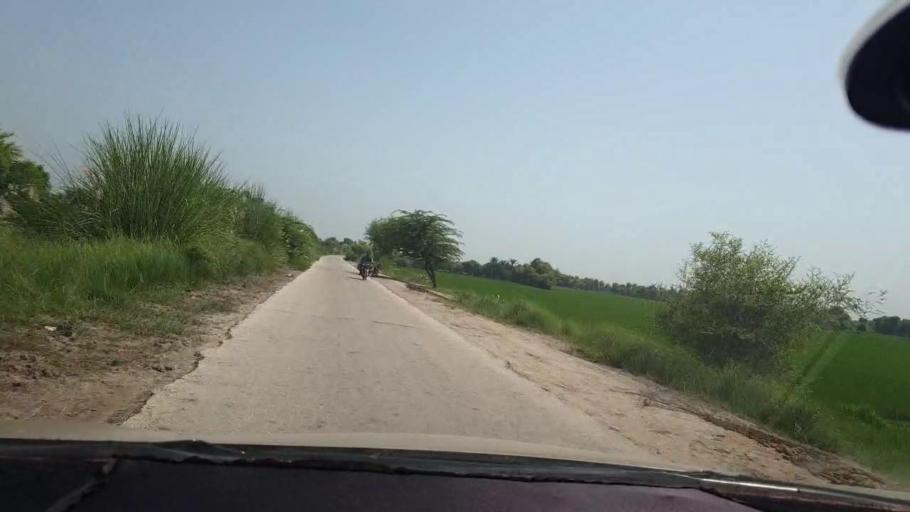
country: PK
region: Sindh
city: Kambar
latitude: 27.5154
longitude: 68.0108
